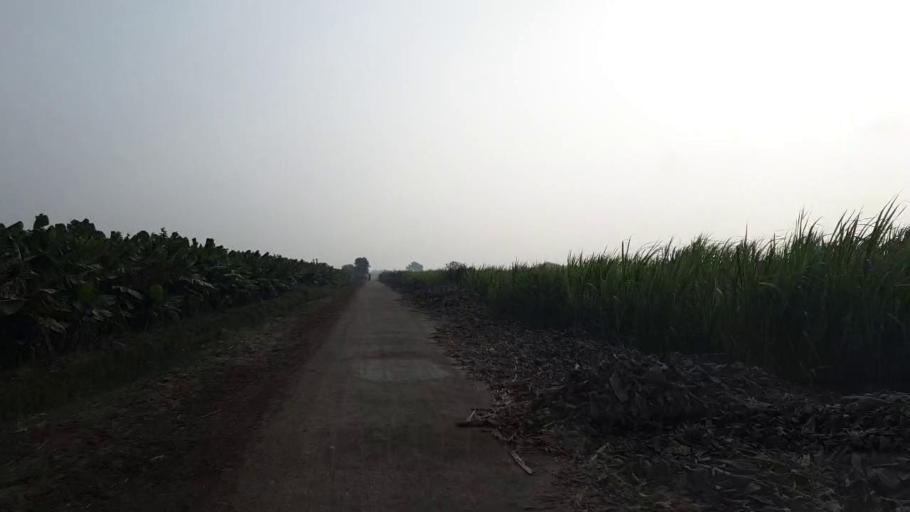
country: PK
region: Sindh
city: Tando Muhammad Khan
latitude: 25.1614
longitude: 68.5871
